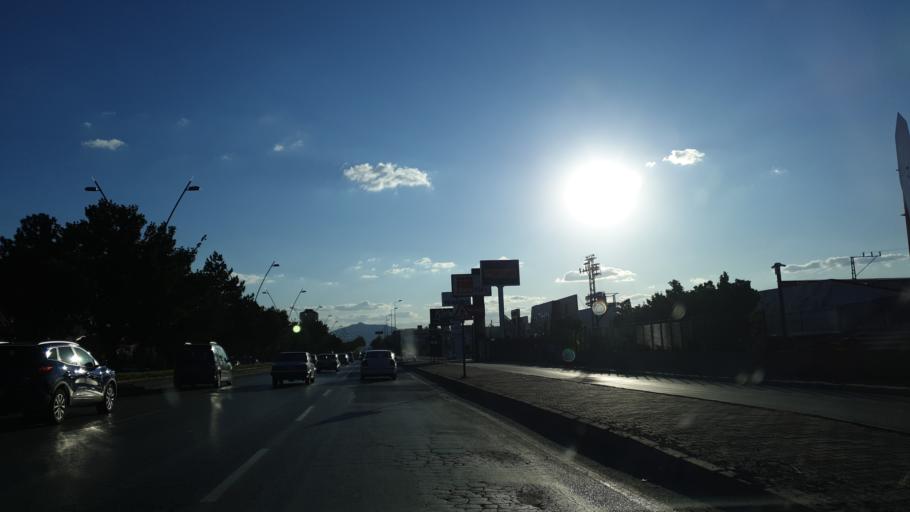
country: TR
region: Kayseri
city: Kocasinan
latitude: 38.7486
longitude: 35.5408
